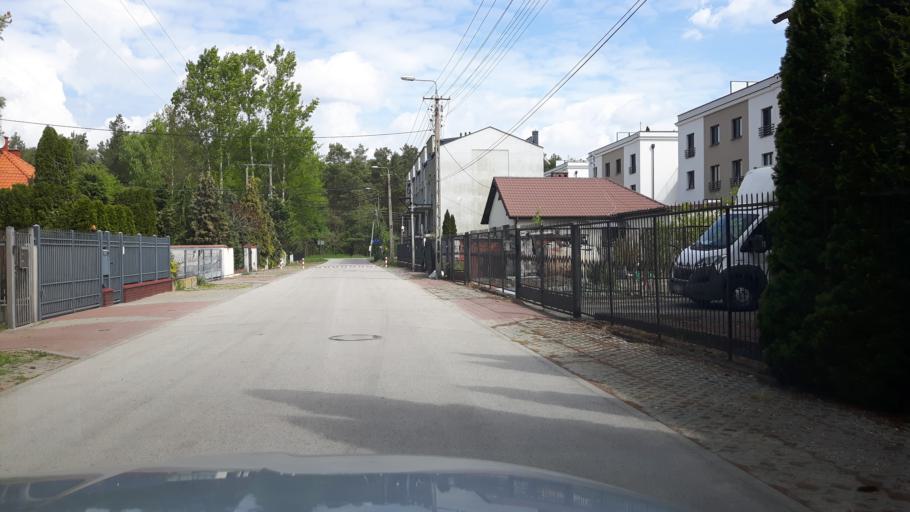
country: PL
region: Masovian Voivodeship
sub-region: Warszawa
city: Wesola
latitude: 52.2513
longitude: 21.2006
